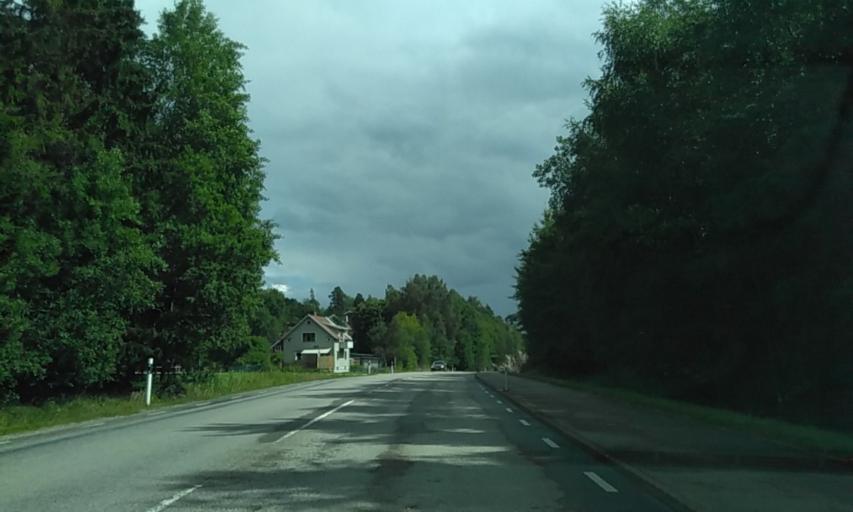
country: SE
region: Vaestra Goetaland
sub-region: Alingsas Kommun
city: Alingsas
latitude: 57.9500
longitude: 12.4968
